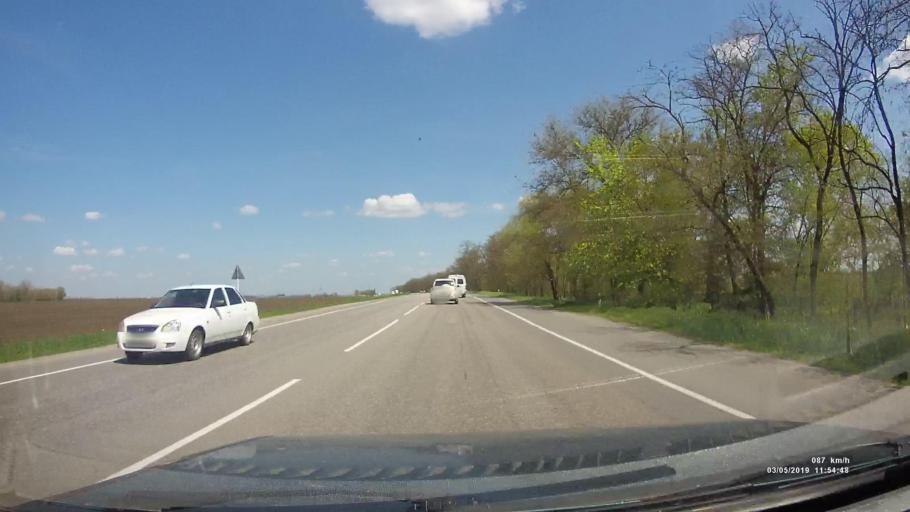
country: RU
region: Rostov
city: Bagayevskaya
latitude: 47.1735
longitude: 40.2850
